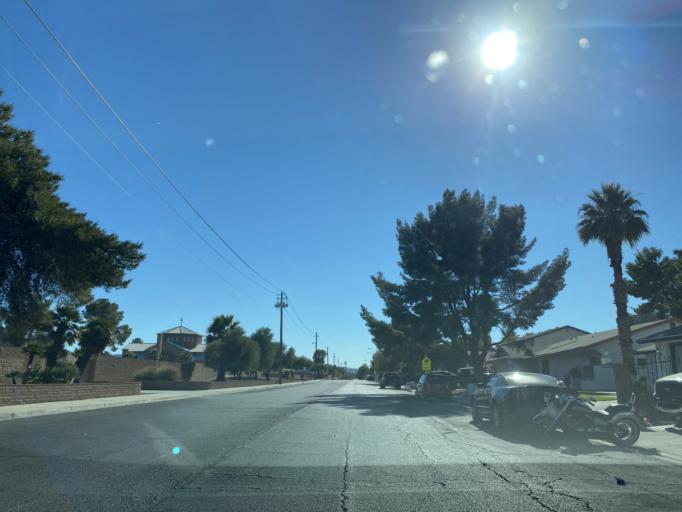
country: US
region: Nevada
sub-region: Clark County
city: Whitney
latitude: 36.0930
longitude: -115.0869
